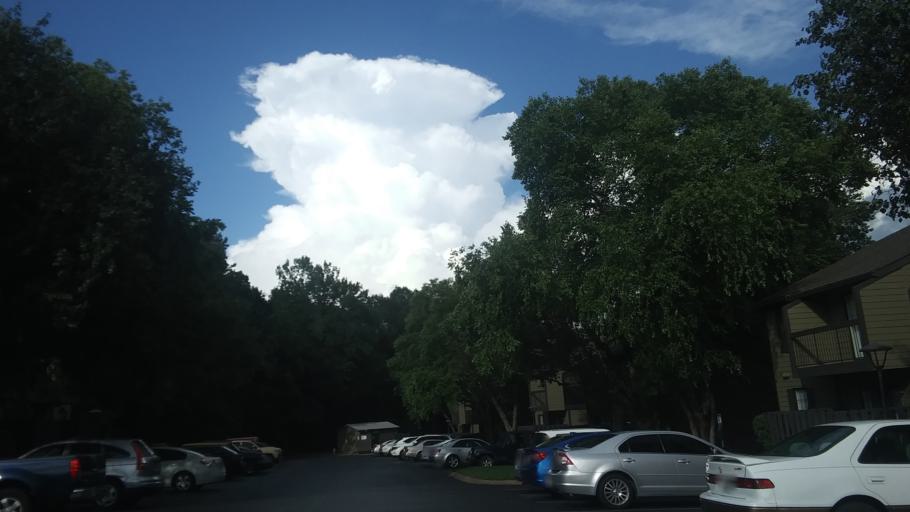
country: US
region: Tennessee
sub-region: Rutherford County
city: La Vergne
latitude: 36.0850
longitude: -86.6438
